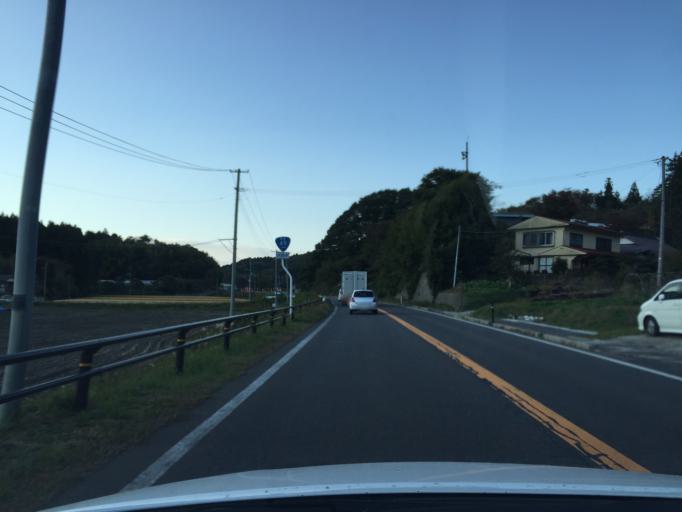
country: JP
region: Fukushima
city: Ishikawa
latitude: 37.2659
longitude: 140.5548
